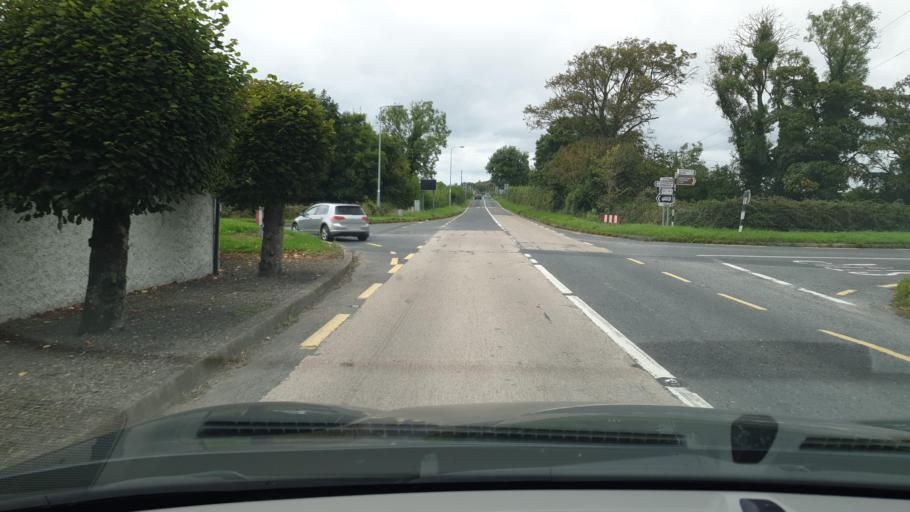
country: IE
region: Leinster
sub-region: Kildare
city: Naas
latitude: 53.2245
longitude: -6.7144
